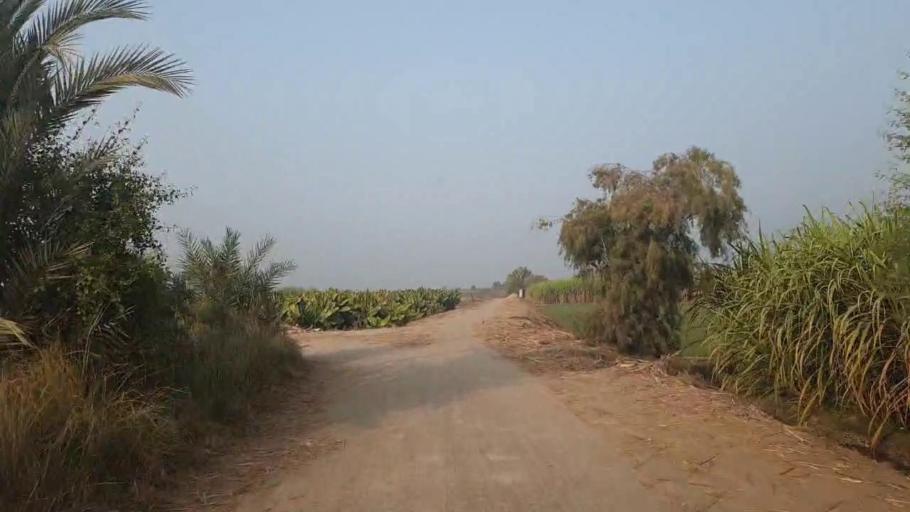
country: PK
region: Sindh
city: Shahdadpur
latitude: 25.8766
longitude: 68.6037
